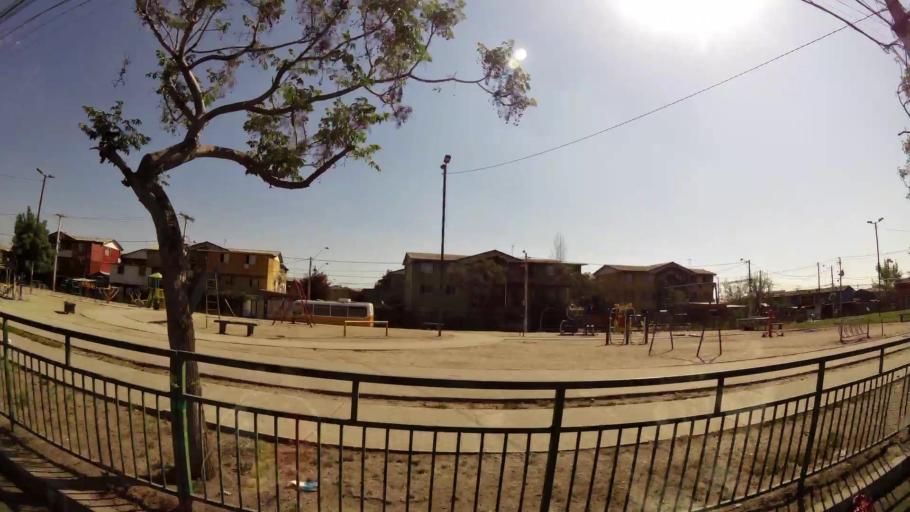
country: CL
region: Santiago Metropolitan
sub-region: Provincia de Santiago
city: La Pintana
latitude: -33.5623
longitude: -70.6250
